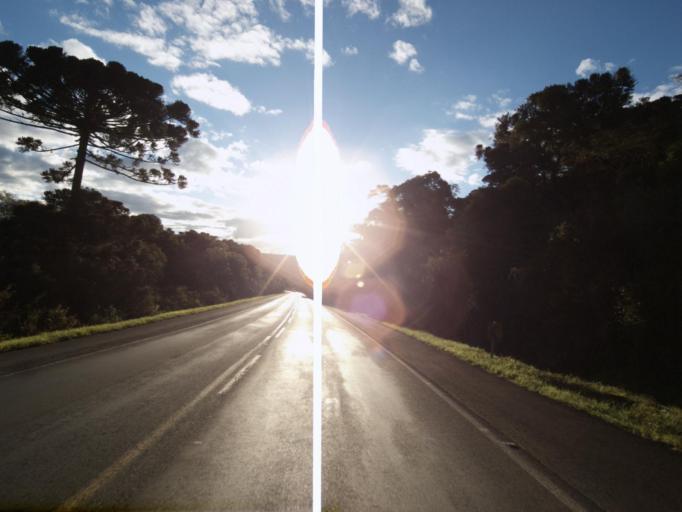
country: BR
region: Santa Catarina
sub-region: Campos Novos
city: Campos Novos
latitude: -27.3327
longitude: -51.3500
